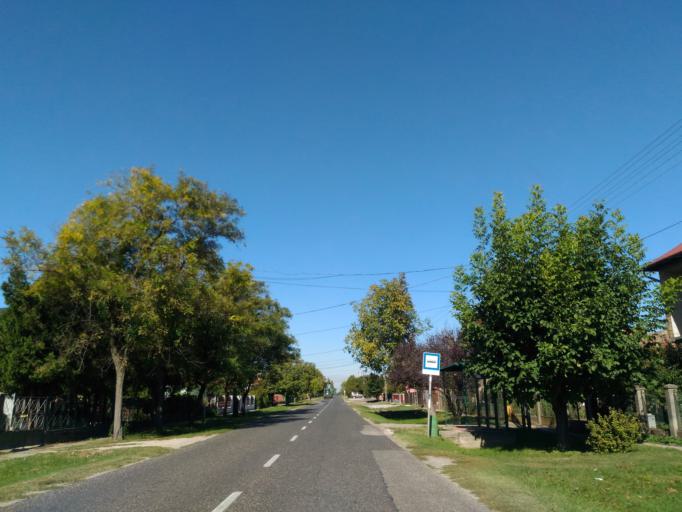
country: HU
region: Fejer
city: Ivancsa
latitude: 47.1669
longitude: 18.8205
